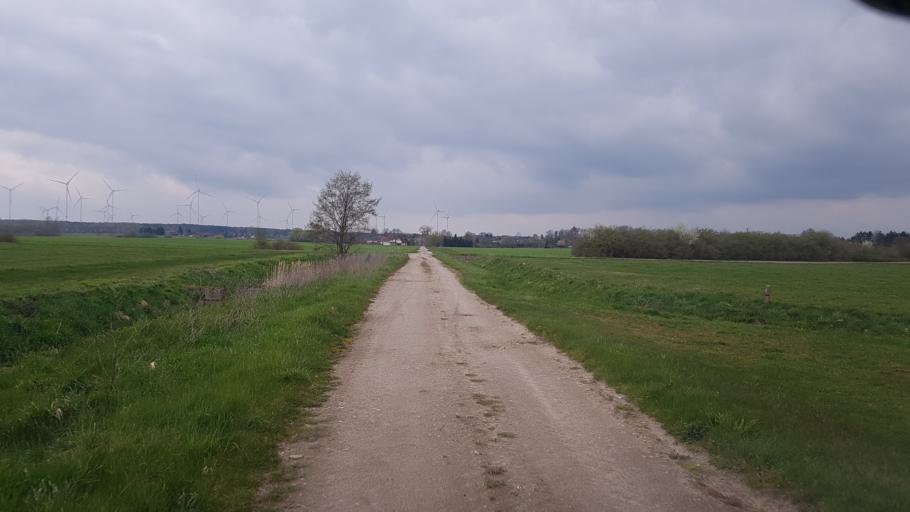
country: DE
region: Brandenburg
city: Sallgast
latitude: 51.6366
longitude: 13.8703
